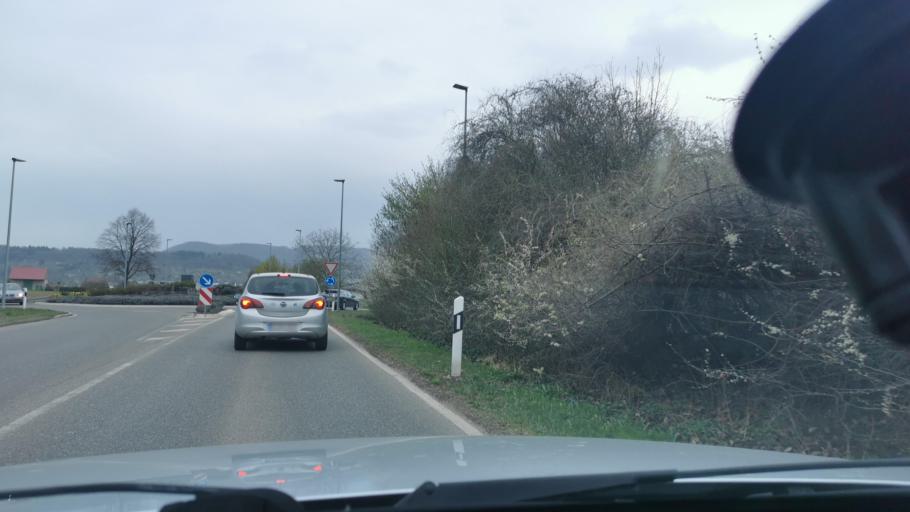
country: DE
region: Baden-Wuerttemberg
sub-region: Regierungsbezirk Stuttgart
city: Holzmaden
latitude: 48.6260
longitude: 9.5251
